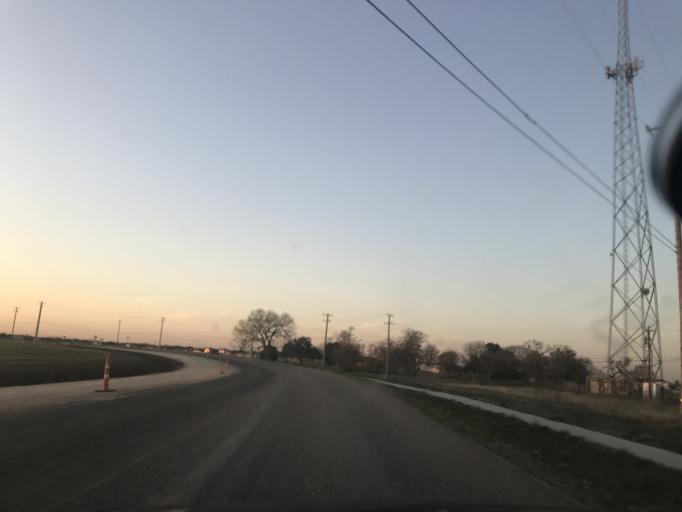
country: US
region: Texas
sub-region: Williamson County
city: Hutto
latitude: 30.5169
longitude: -97.5366
